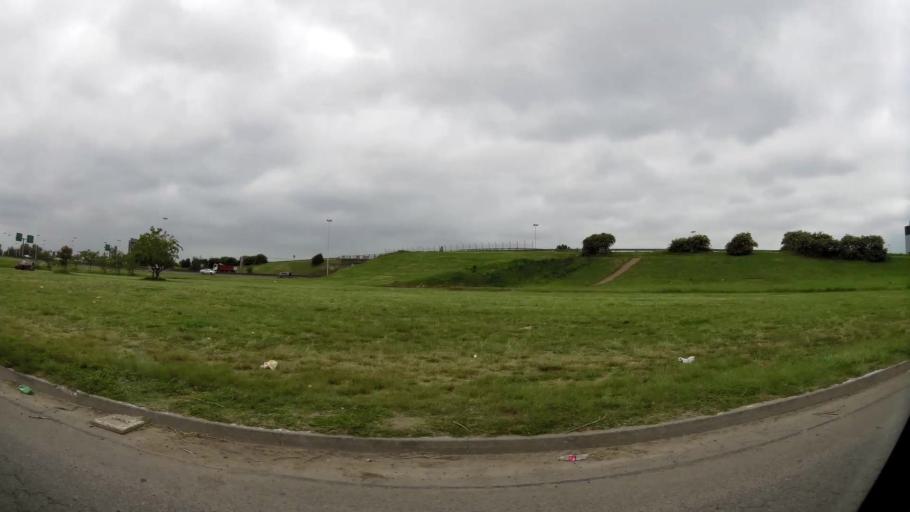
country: AR
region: Buenos Aires
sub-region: Partido de Ezeiza
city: Ezeiza
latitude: -34.8346
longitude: -58.5082
